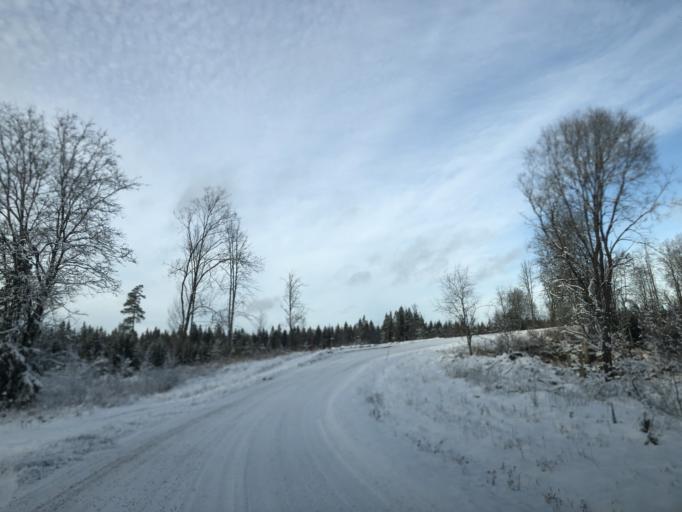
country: SE
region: Vaestra Goetaland
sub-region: Ulricehamns Kommun
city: Ulricehamn
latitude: 57.7625
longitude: 13.5165
